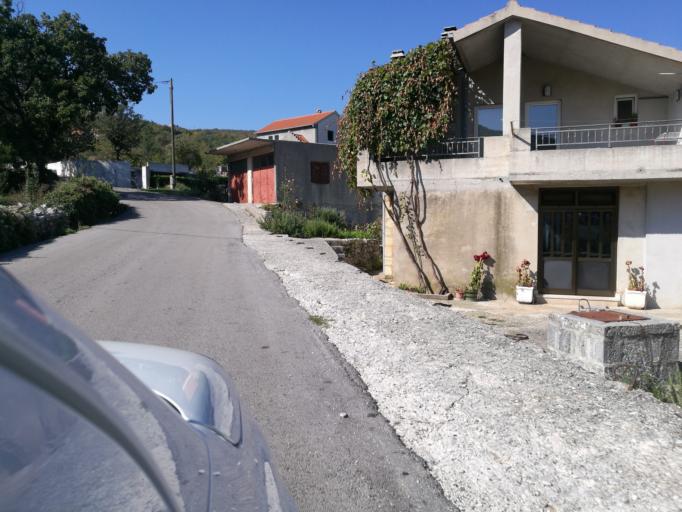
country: HR
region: Splitsko-Dalmatinska
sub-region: Grad Omis
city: Omis
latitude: 43.5149
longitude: 16.7334
